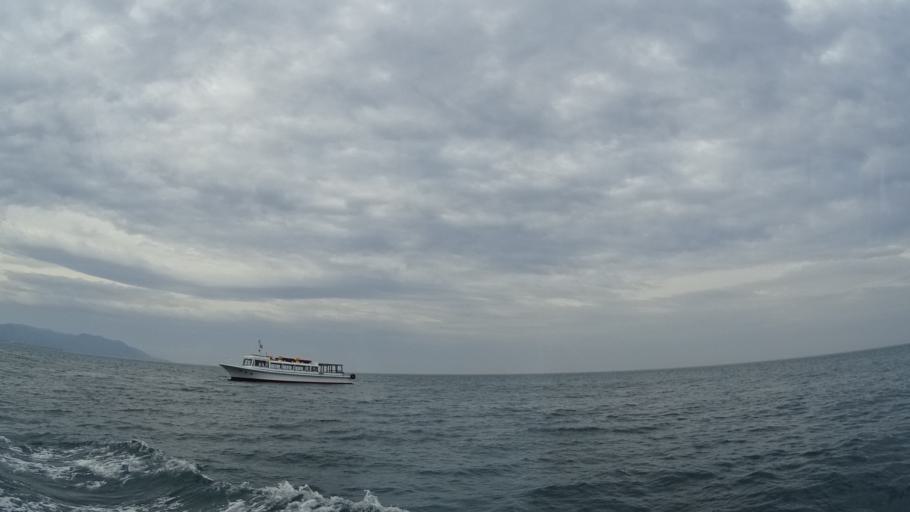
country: JP
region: Fukui
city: Mikuni
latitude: 36.2391
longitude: 136.1242
